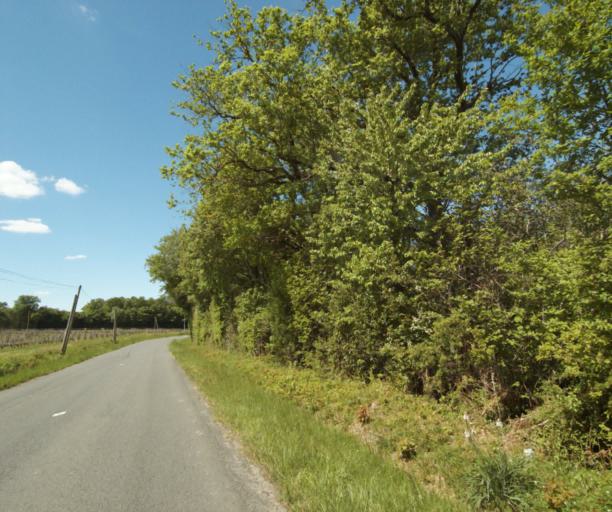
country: FR
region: Poitou-Charentes
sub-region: Departement de la Charente-Maritime
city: Burie
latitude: 45.7641
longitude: -0.4813
